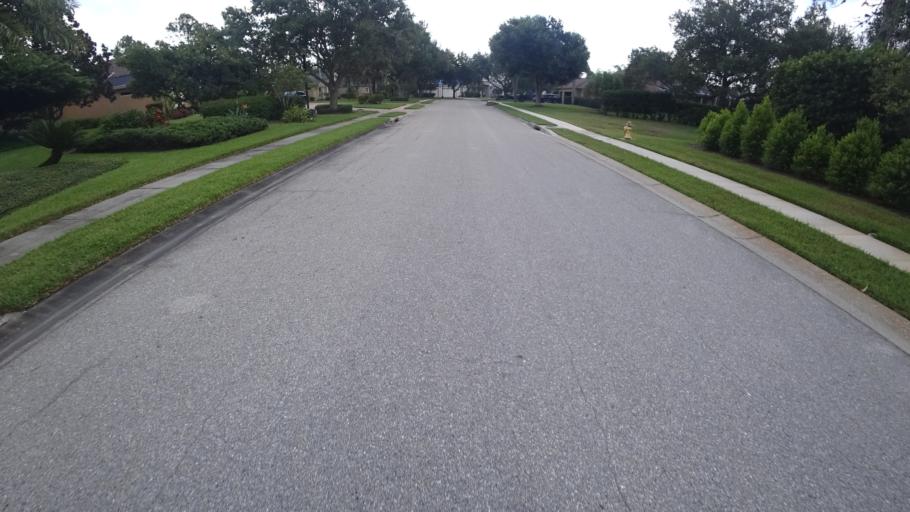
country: US
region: Florida
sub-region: Sarasota County
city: The Meadows
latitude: 27.4097
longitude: -82.4341
